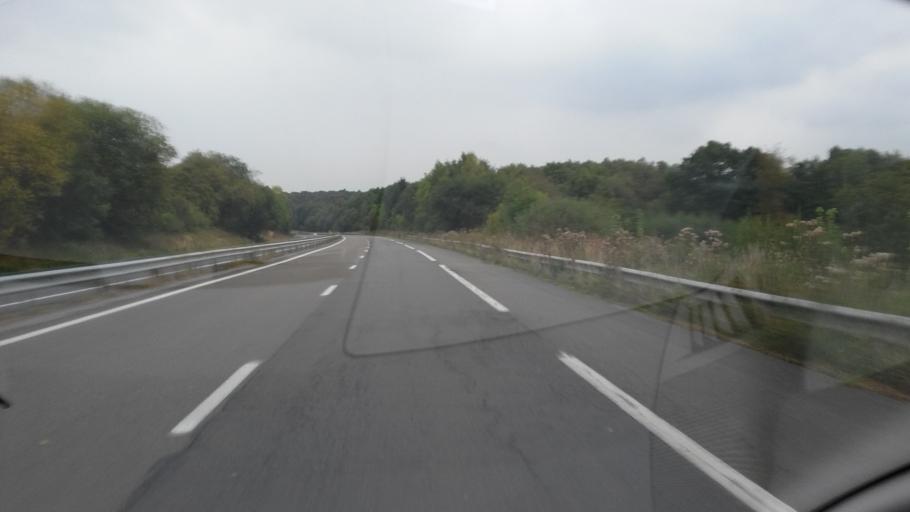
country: FR
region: Champagne-Ardenne
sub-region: Departement des Ardennes
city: Douzy
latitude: 49.7328
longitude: 5.0176
